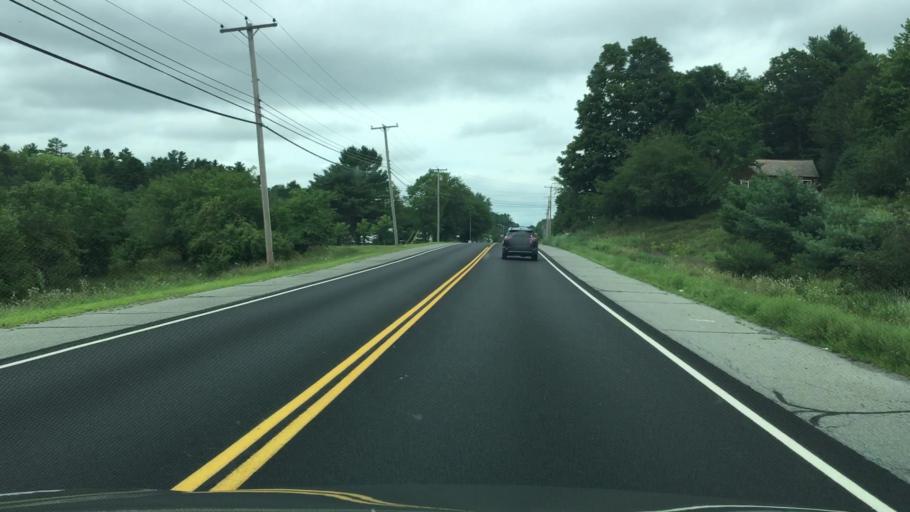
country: US
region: Maine
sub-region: Penobscot County
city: Orrington
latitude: 44.6993
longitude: -68.8204
